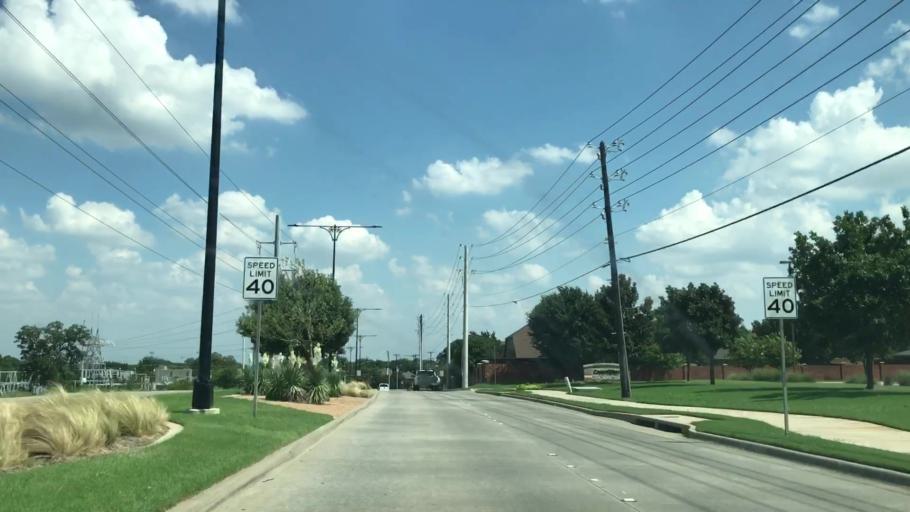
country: US
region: Texas
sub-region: Dallas County
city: Coppell
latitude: 32.9730
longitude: -97.0142
